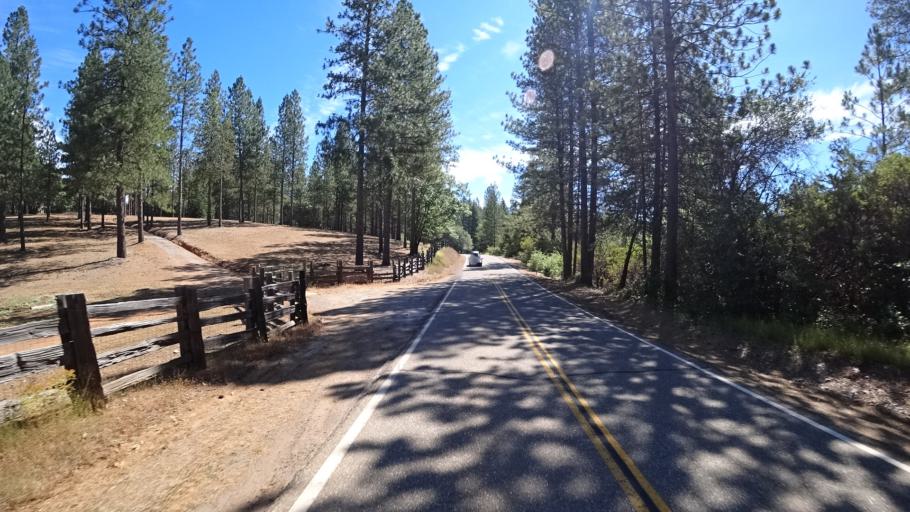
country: US
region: California
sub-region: Amador County
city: Pioneer
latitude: 38.3379
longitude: -120.5633
